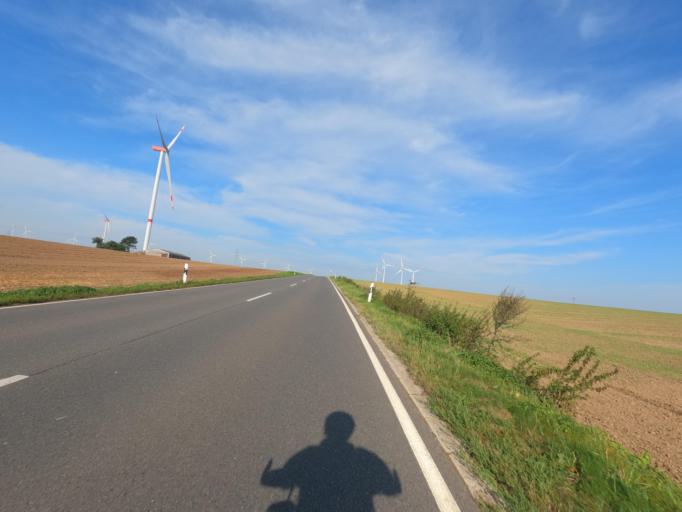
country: DE
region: North Rhine-Westphalia
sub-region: Regierungsbezirk Koln
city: Linnich
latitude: 50.9830
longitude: 6.2487
